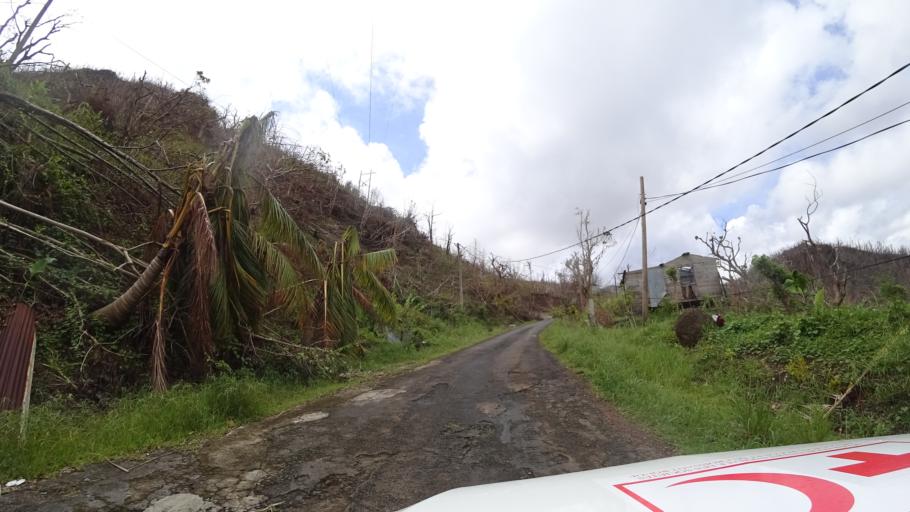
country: DM
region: Saint David
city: Castle Bruce
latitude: 15.4007
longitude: -61.2558
